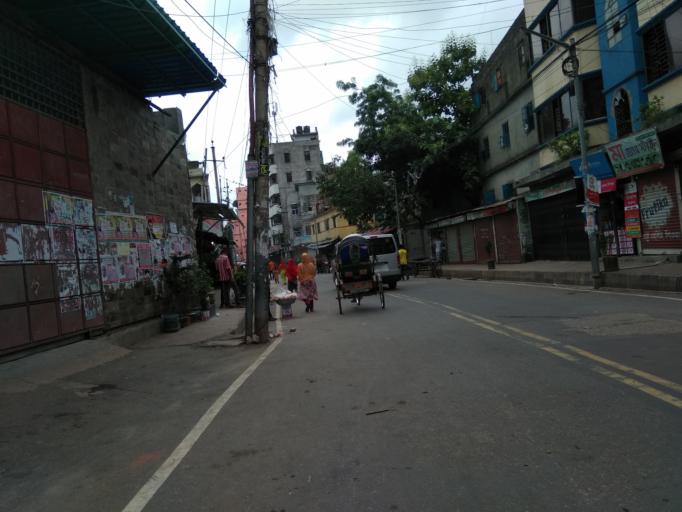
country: BD
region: Dhaka
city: Tungi
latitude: 23.8166
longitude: 90.3619
